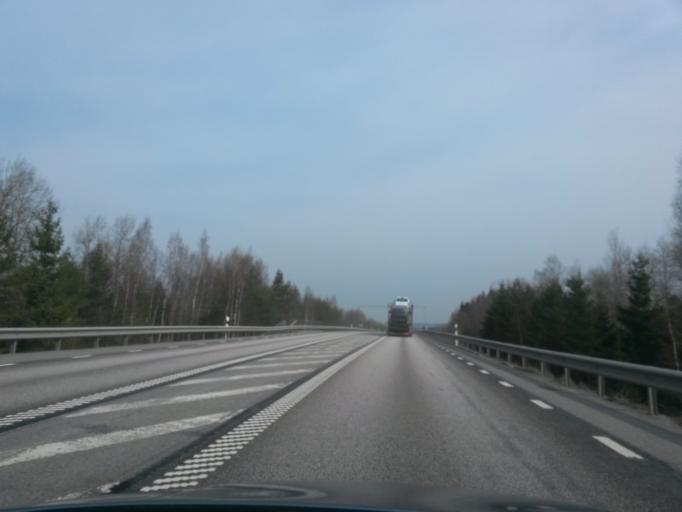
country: SE
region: Vaestra Goetaland
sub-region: Gullspangs Kommun
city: Hova
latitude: 58.8479
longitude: 14.1979
